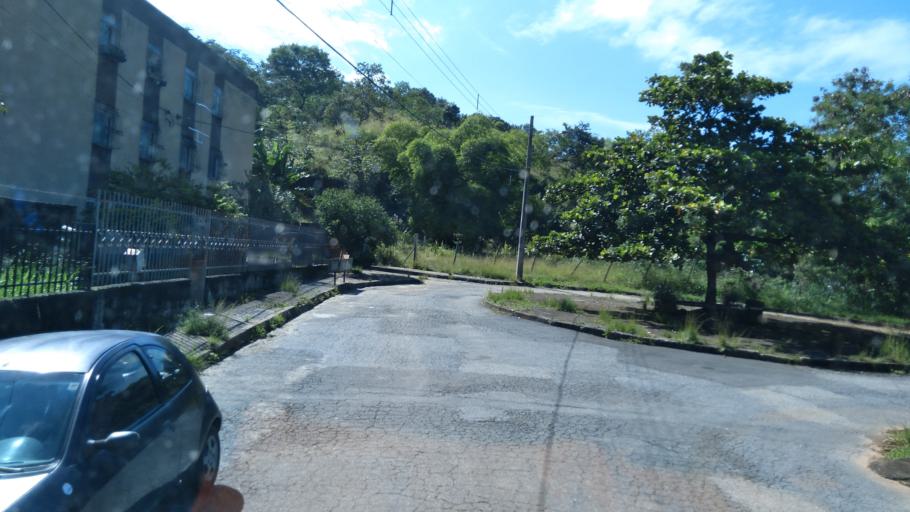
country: BR
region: Minas Gerais
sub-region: Santa Luzia
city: Santa Luzia
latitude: -19.8271
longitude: -43.9037
